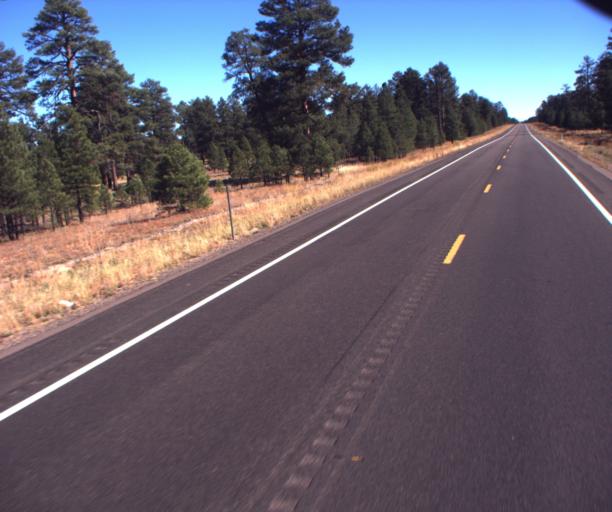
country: US
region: Arizona
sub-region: Apache County
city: Saint Michaels
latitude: 35.6962
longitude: -109.2750
